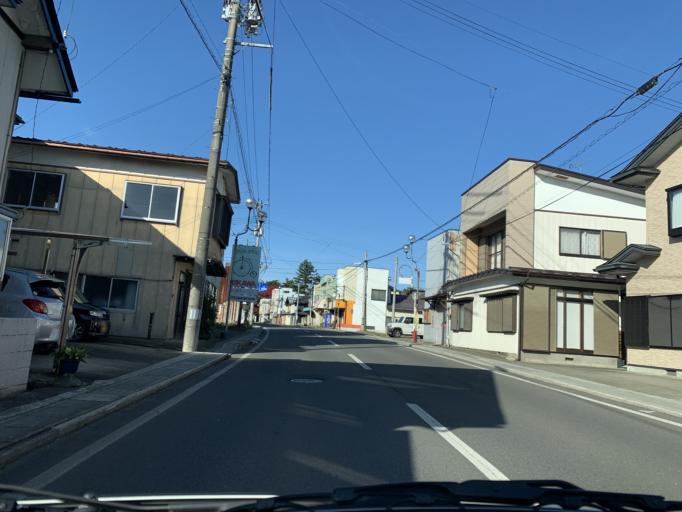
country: JP
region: Iwate
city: Mizusawa
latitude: 39.1946
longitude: 141.1190
